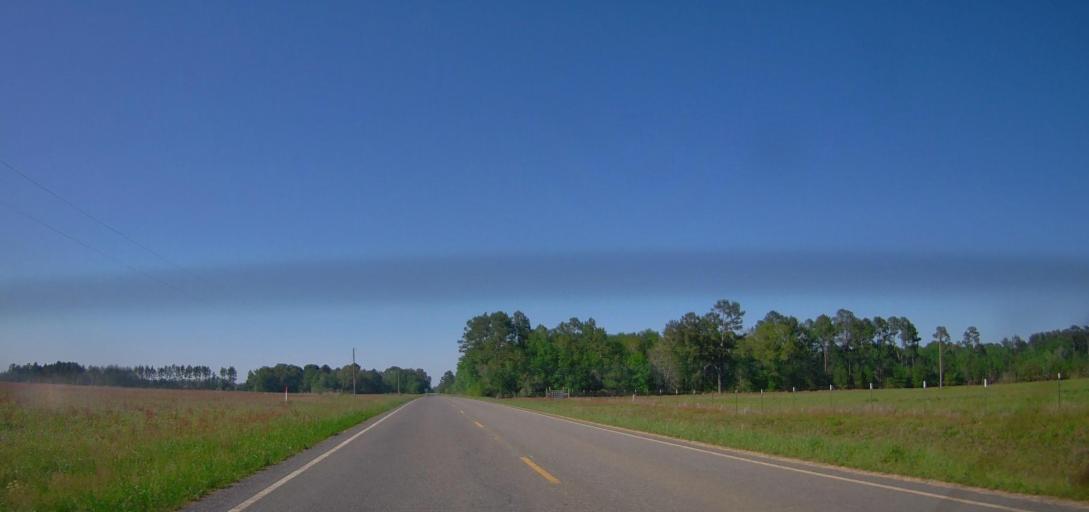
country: US
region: Georgia
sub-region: Wilcox County
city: Rochelle
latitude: 32.0796
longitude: -83.5035
